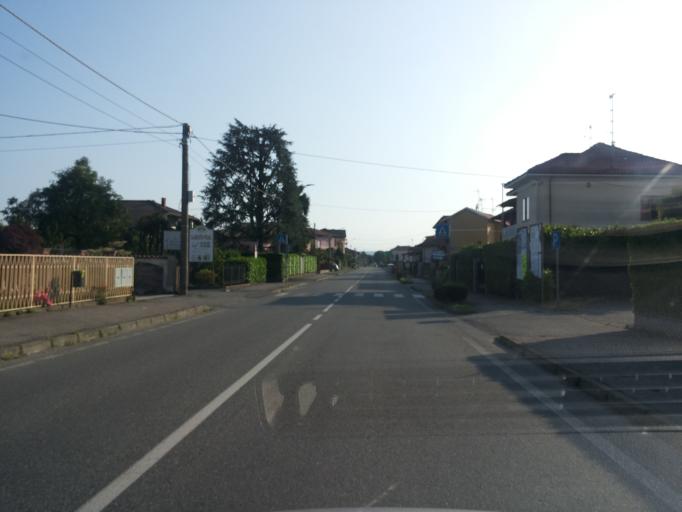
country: IT
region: Piedmont
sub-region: Provincia di Biella
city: Candelo
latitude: 45.5340
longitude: 8.1041
